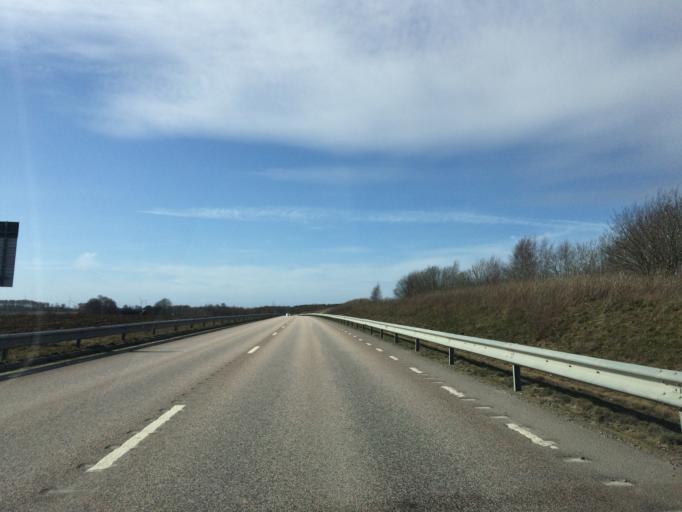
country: SE
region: Halland
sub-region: Laholms Kommun
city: Veinge
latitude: 56.5437
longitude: 13.0862
